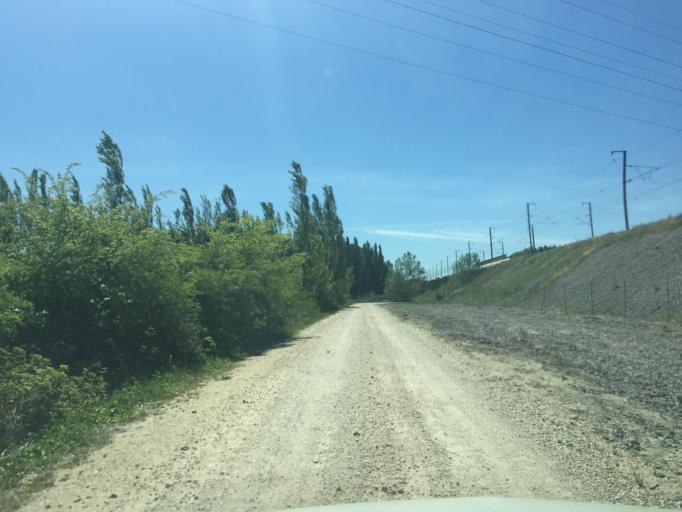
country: FR
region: Languedoc-Roussillon
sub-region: Departement du Gard
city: Montfaucon
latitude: 44.0823
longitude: 4.7706
